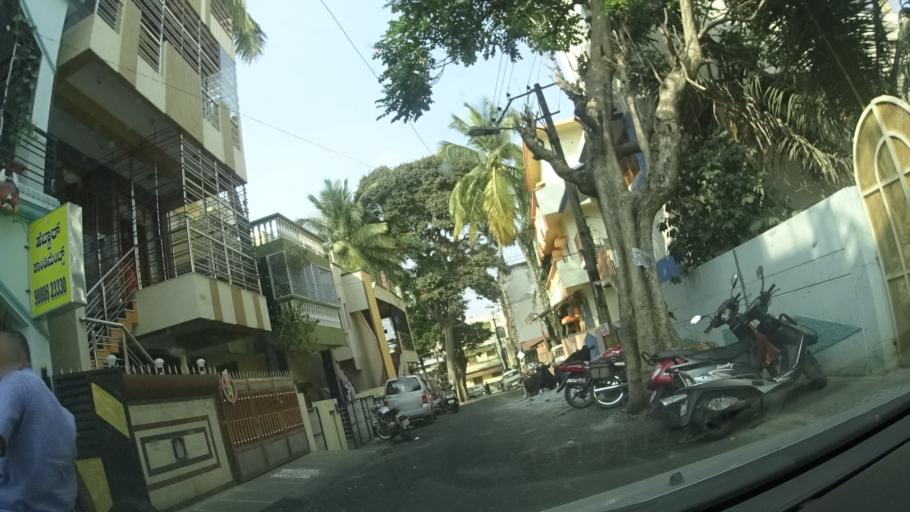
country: IN
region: Karnataka
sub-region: Bangalore Urban
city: Bangalore
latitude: 12.9450
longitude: 77.5604
